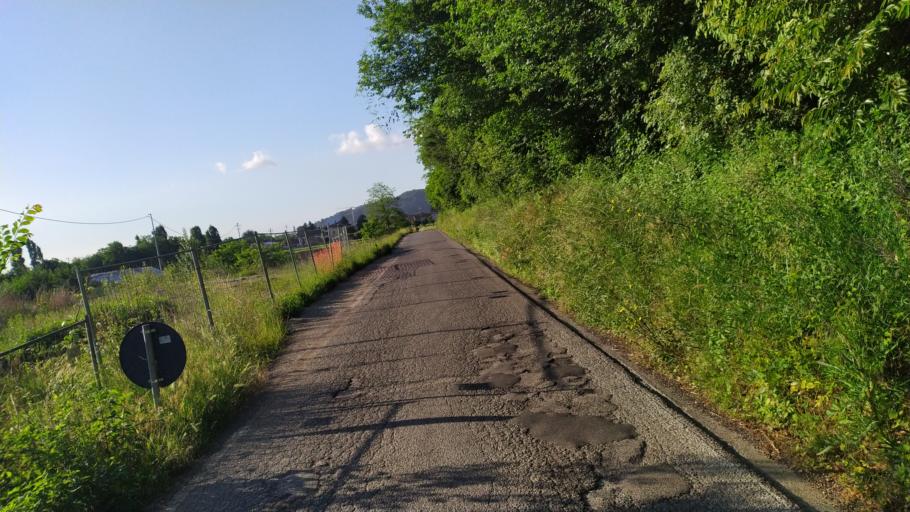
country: IT
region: Veneto
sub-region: Provincia di Vicenza
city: Malo
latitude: 45.6445
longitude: 11.4206
